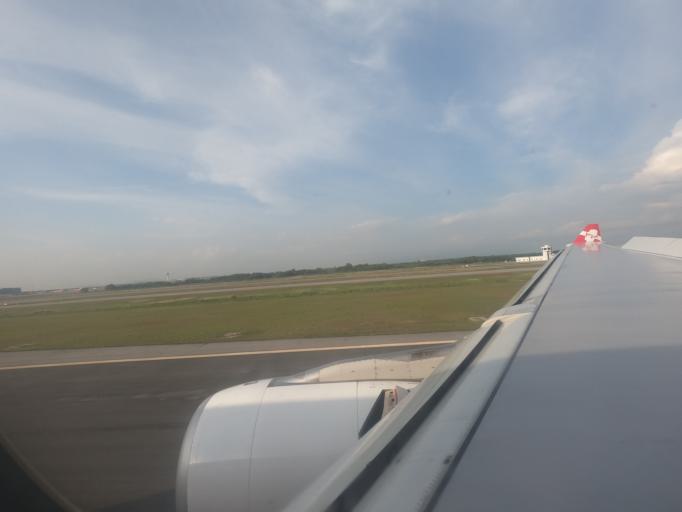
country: MY
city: Sungai Pelek New Village
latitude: 2.7241
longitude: 101.6869
